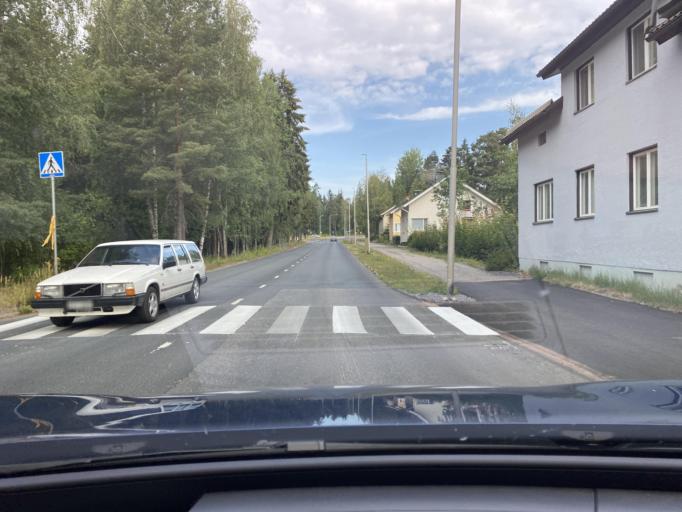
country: FI
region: Pirkanmaa
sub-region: Lounais-Pirkanmaa
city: Vammala
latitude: 61.3534
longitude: 22.8941
